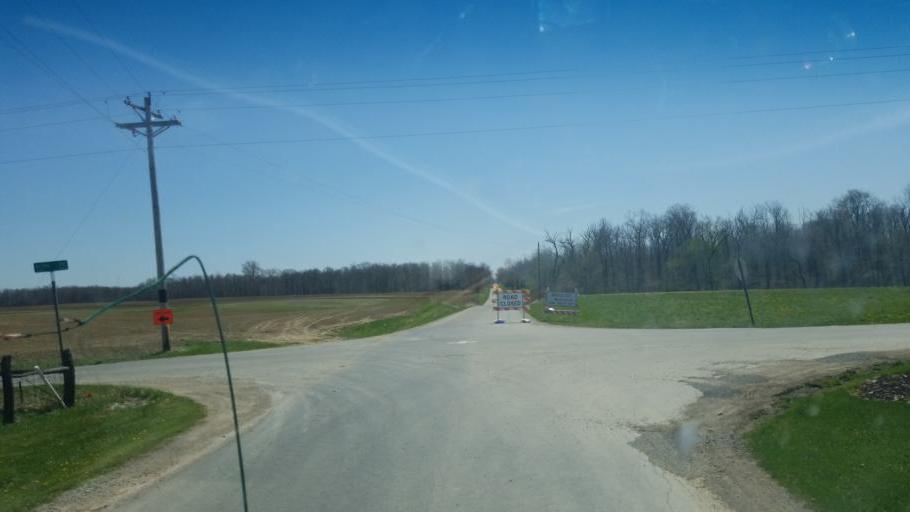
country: US
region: Ohio
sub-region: Huron County
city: Greenwich
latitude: 41.0483
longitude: -82.5115
